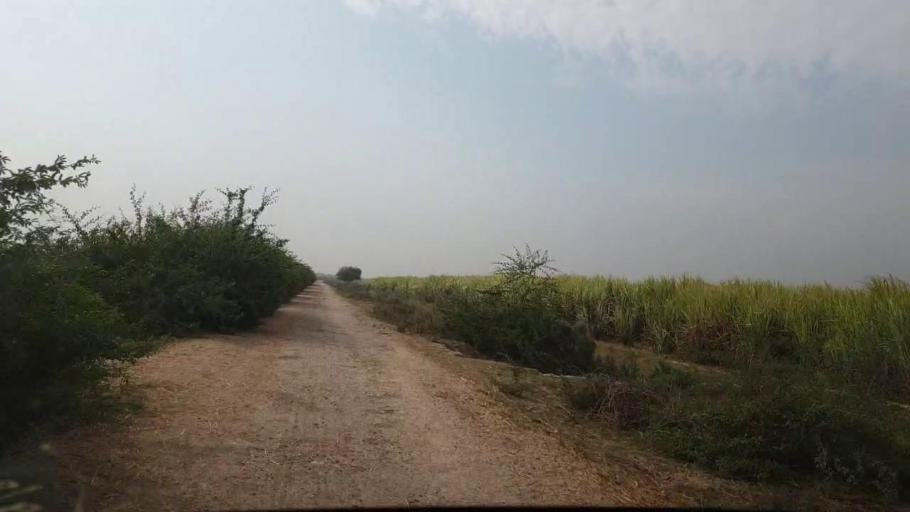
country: PK
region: Sindh
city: Chuhar Jamali
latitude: 24.4130
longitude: 67.9387
